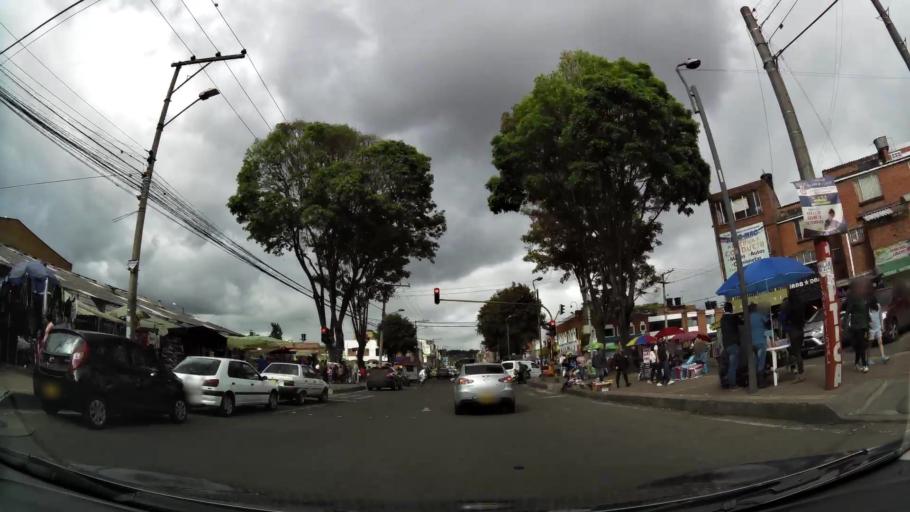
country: CO
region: Bogota D.C.
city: Barrio San Luis
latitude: 4.7081
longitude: -74.1051
